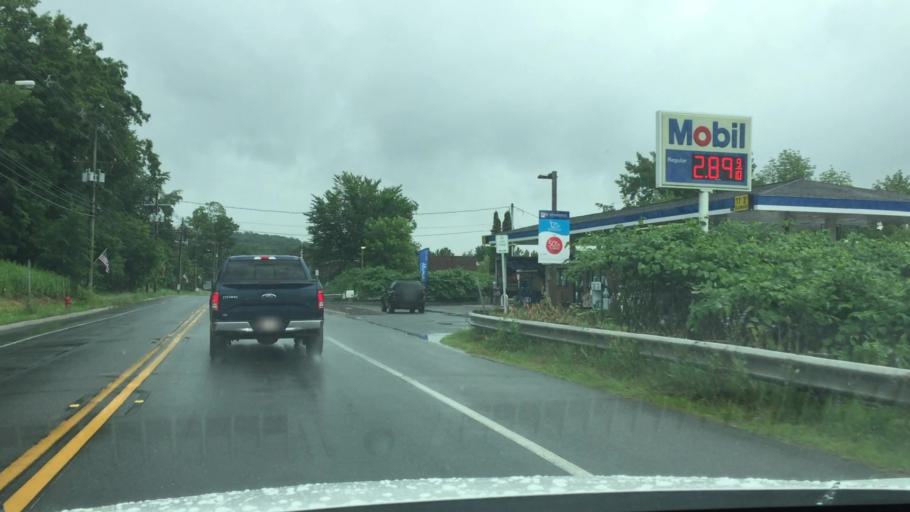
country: US
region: Massachusetts
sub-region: Berkshire County
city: Lanesborough
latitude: 42.5214
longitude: -73.2283
